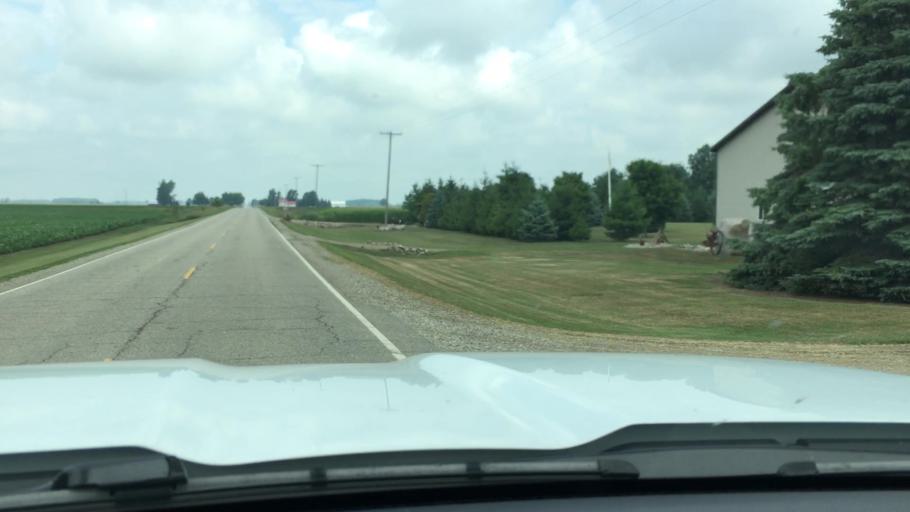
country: US
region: Michigan
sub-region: Sanilac County
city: Marlette
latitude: 43.3677
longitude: -83.0060
